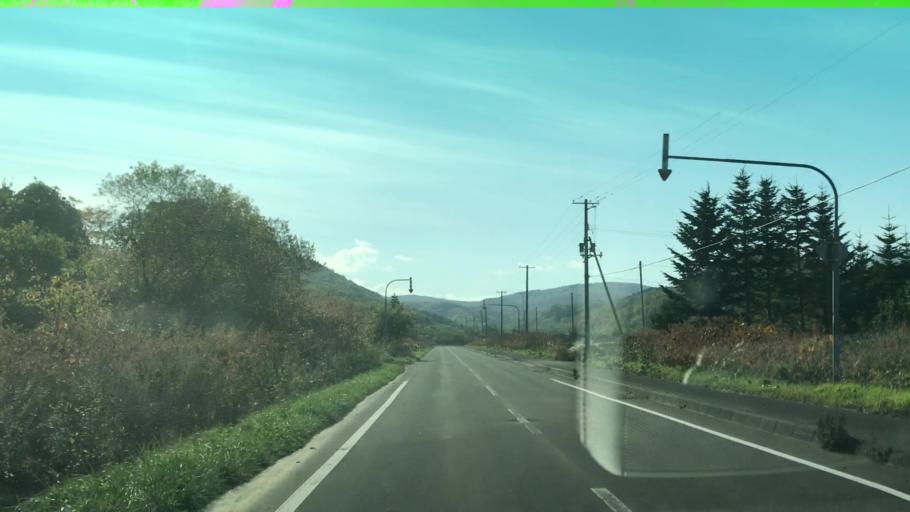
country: JP
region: Hokkaido
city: Yoichi
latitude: 43.1597
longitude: 140.8220
